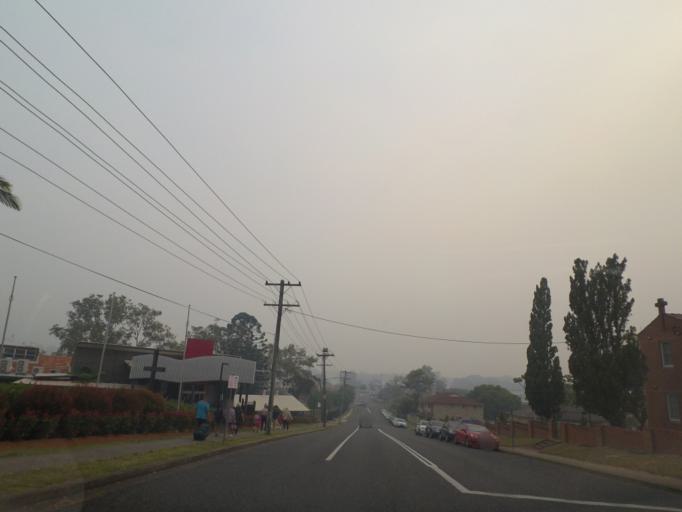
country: AU
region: New South Wales
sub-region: Coffs Harbour
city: Coffs Harbour
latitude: -30.3012
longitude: 153.1133
